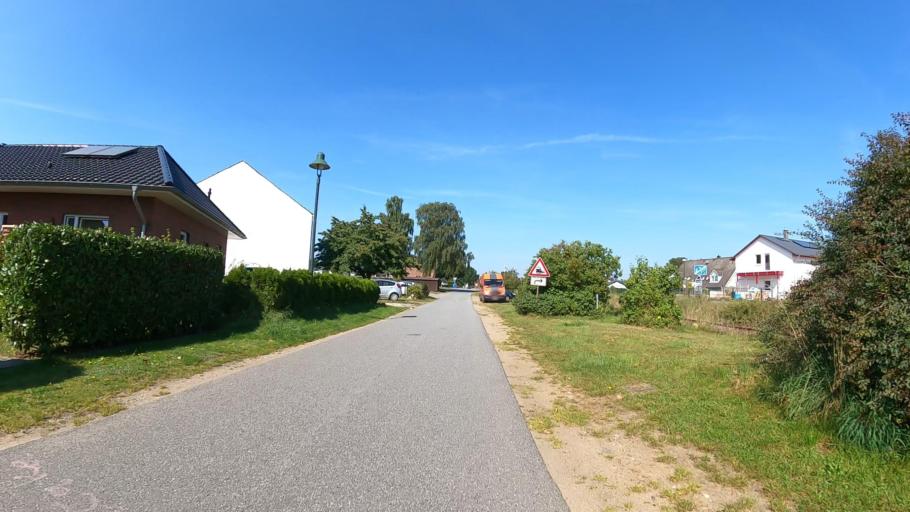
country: DE
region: Schleswig-Holstein
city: Nutzen
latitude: 53.8620
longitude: 9.9182
